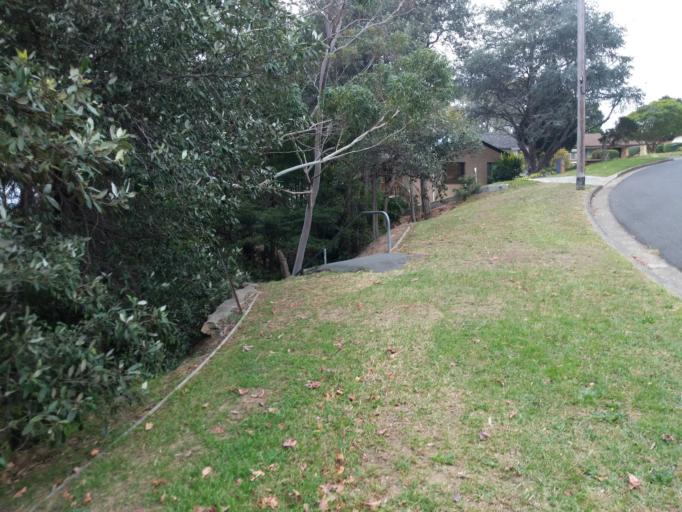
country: AU
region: New South Wales
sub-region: Sutherland Shire
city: Kirrawee
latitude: -34.0273
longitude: 151.0714
